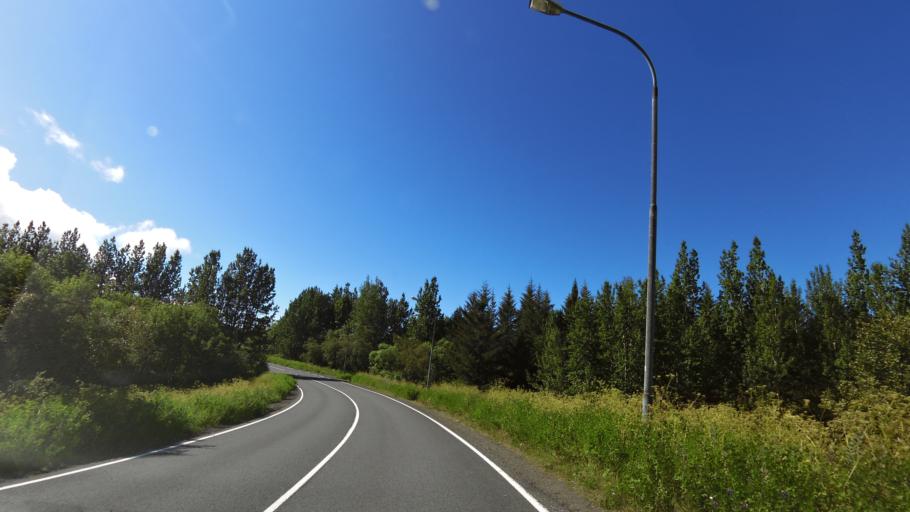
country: IS
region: Capital Region
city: Mosfellsbaer
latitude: 64.1622
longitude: -21.6697
